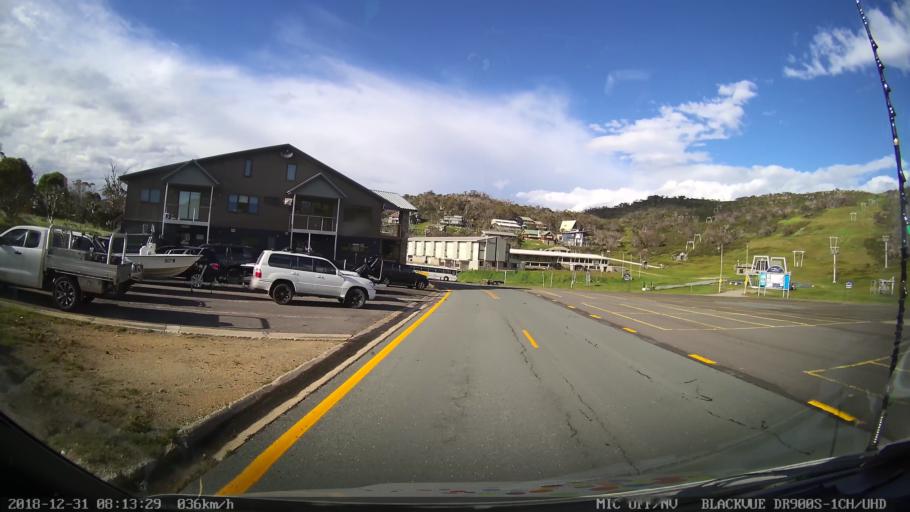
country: AU
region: New South Wales
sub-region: Snowy River
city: Jindabyne
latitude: -36.3917
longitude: 148.4278
